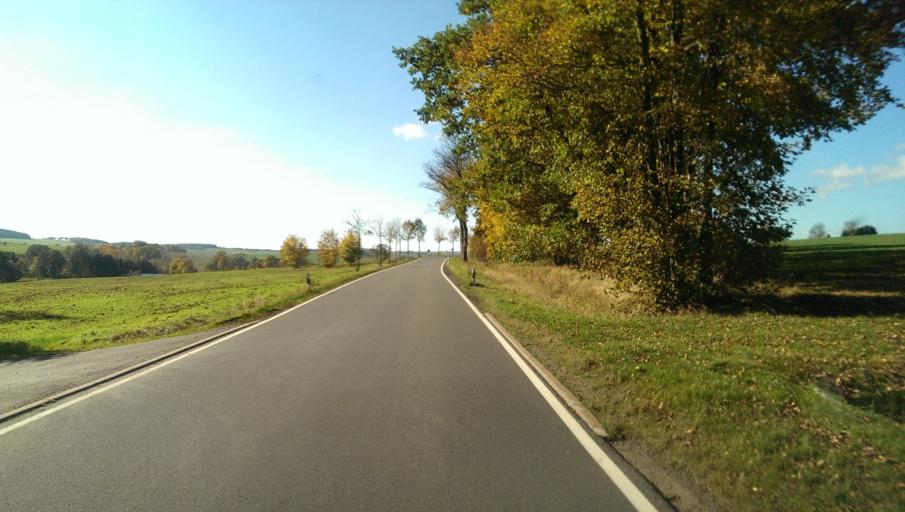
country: DE
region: Saxony
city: Grosshartmannsdorf
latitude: 50.7968
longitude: 13.2910
